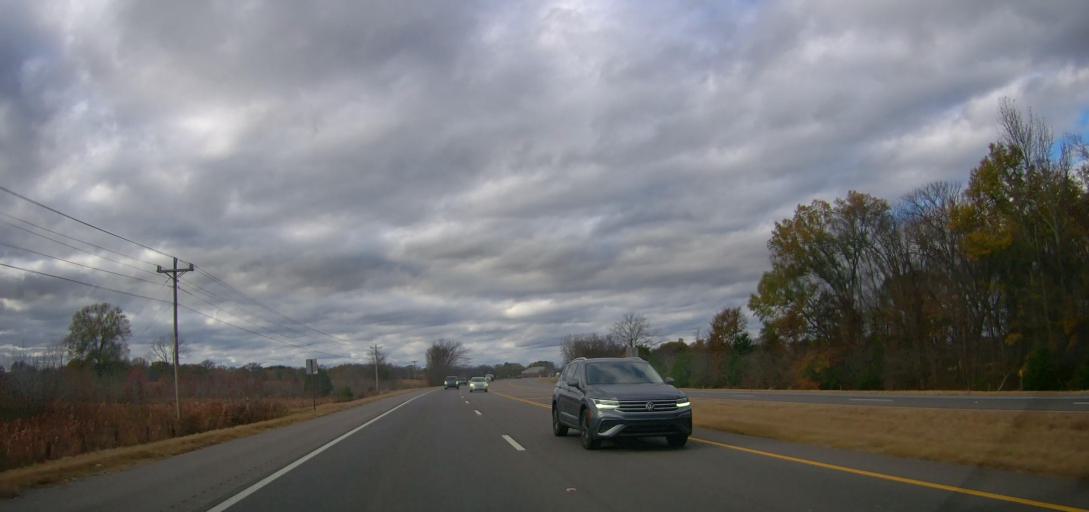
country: US
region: Alabama
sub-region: Lawrence County
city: Moulton
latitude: 34.4688
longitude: -87.2644
